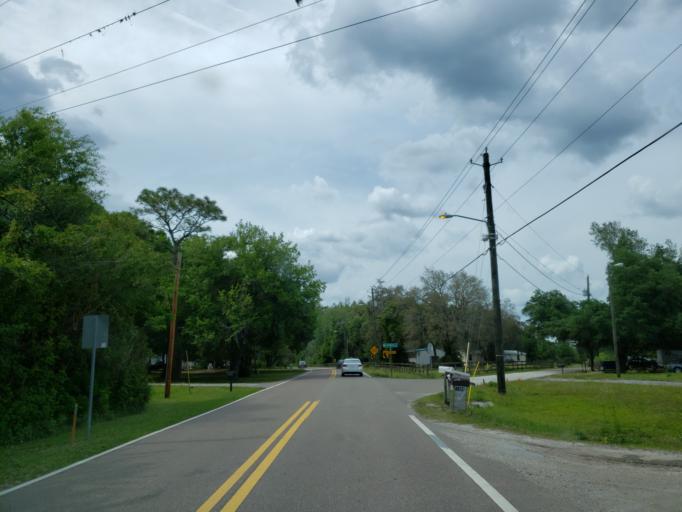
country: US
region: Florida
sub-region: Hillsborough County
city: Keystone
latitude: 28.1290
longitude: -82.6161
